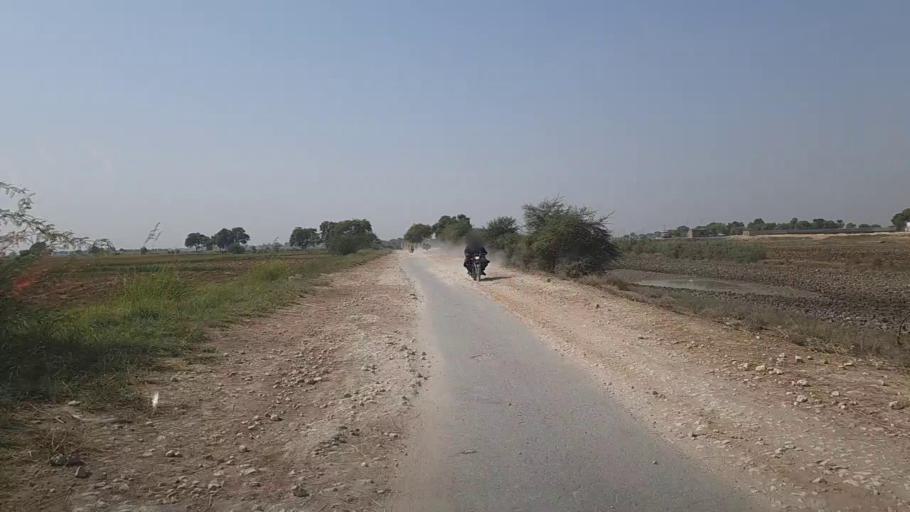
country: PK
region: Sindh
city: Kandhkot
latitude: 28.3887
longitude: 69.3302
